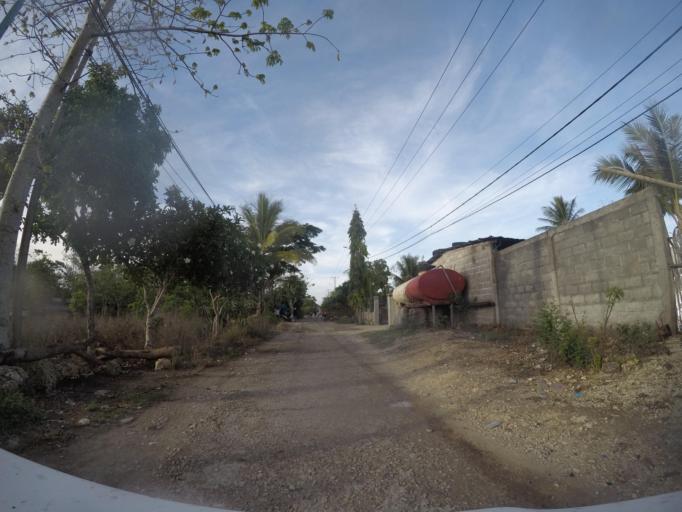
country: TL
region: Baucau
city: Baucau
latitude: -8.4864
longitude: 126.4523
